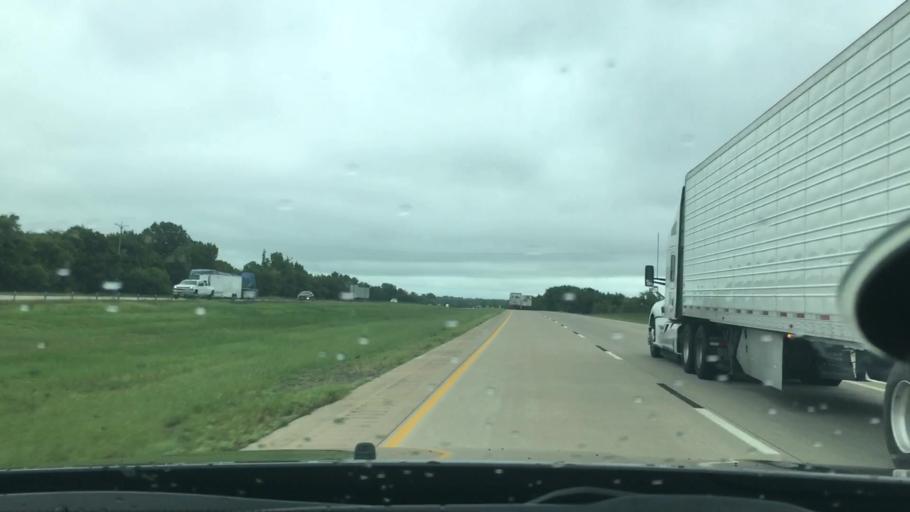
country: US
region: Oklahoma
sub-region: McIntosh County
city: Checotah
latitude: 35.4555
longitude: -95.6426
